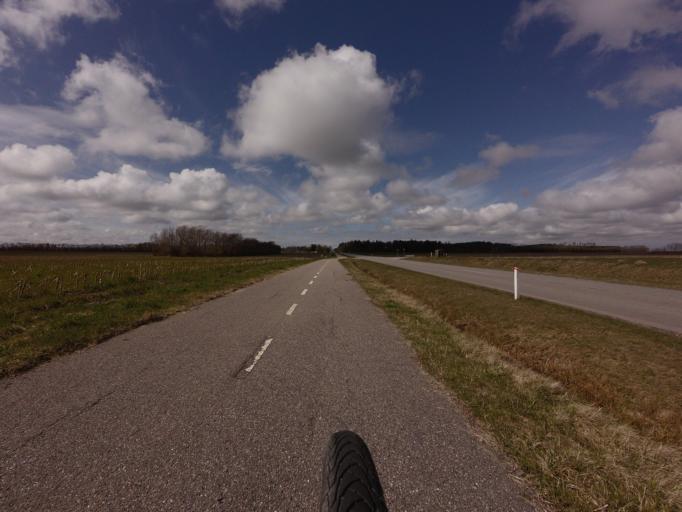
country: DK
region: North Denmark
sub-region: Hjorring Kommune
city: Vra
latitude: 57.3550
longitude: 9.8915
